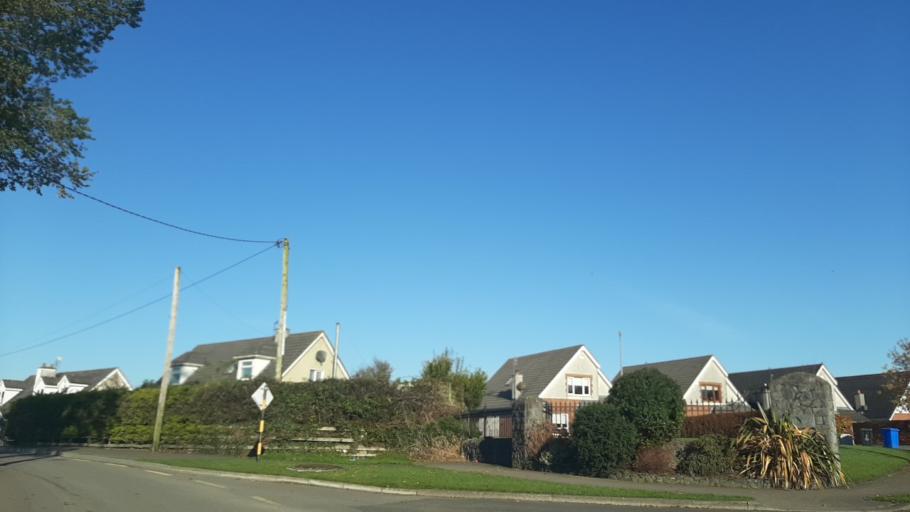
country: IE
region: Leinster
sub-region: Kildare
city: Rathangan
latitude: 53.2177
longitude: -7.0002
